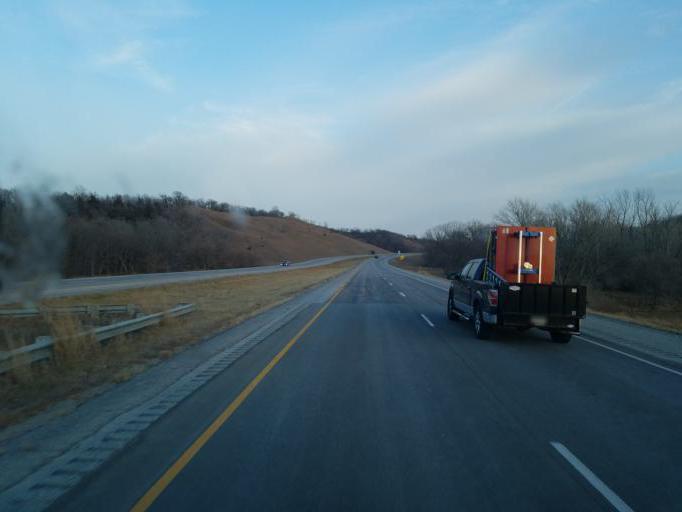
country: US
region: Iowa
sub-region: Harrison County
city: Missouri Valley
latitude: 41.4950
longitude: -95.8907
